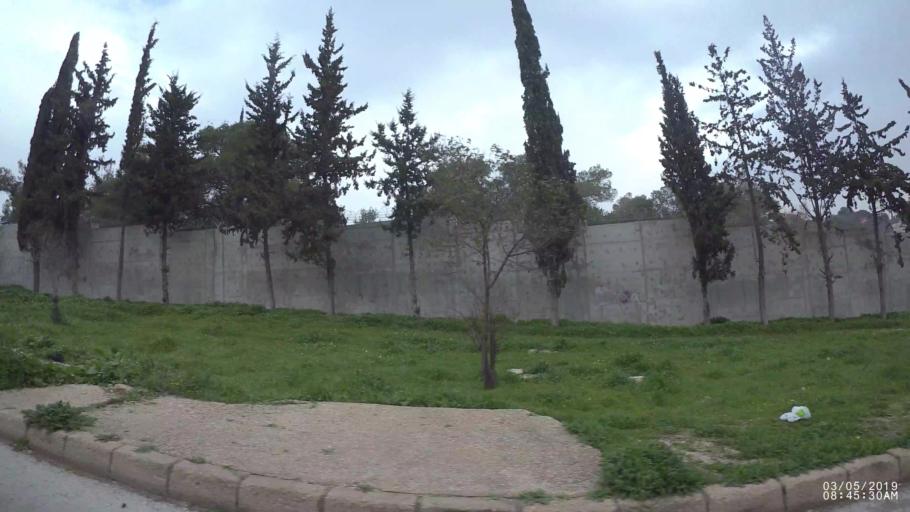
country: JO
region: Amman
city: Amman
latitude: 31.9591
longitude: 35.9436
